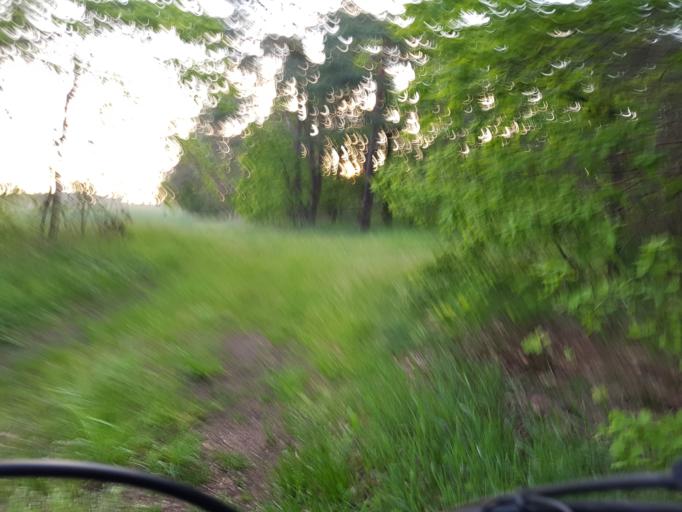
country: DE
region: Brandenburg
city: Bad Liebenwerda
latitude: 51.5567
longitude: 13.4008
